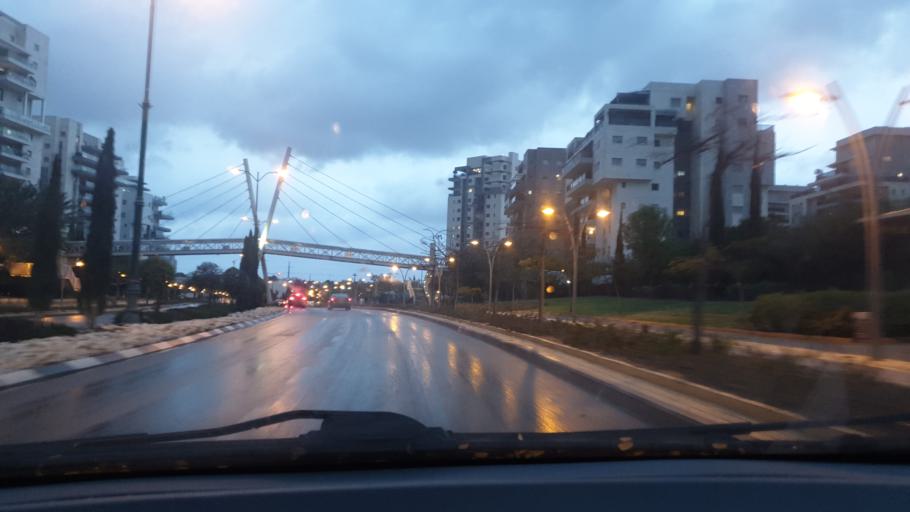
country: IL
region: Central District
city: Rishon LeZiyyon
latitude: 31.9819
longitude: 34.8057
